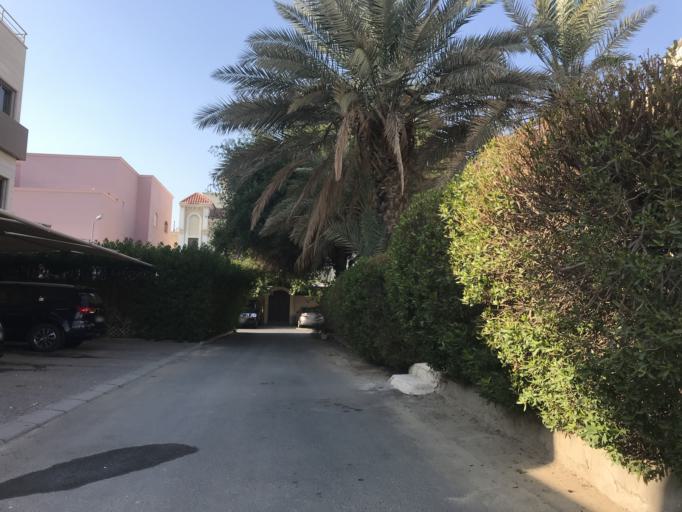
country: KW
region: Al Asimah
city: Ad Dasmah
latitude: 29.3518
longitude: 48.0046
